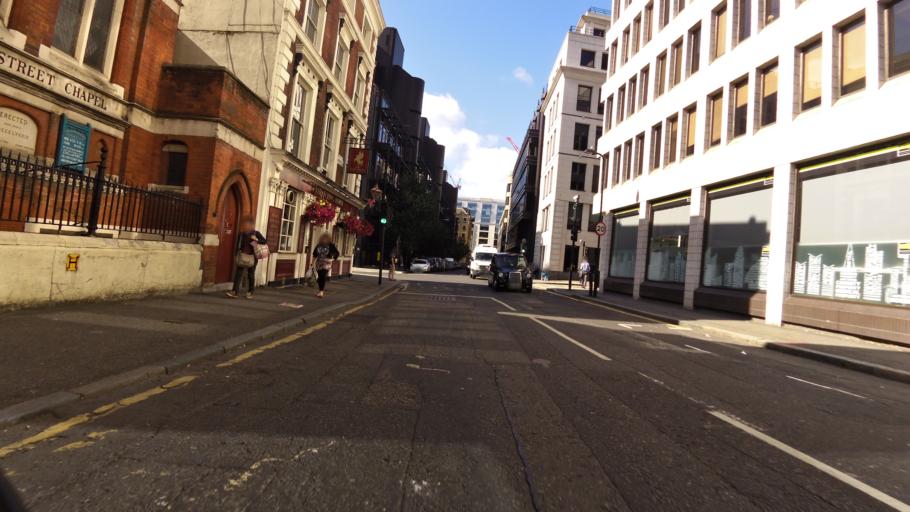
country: GB
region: England
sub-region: Greater London
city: Barbican
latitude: 51.5205
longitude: -0.0851
